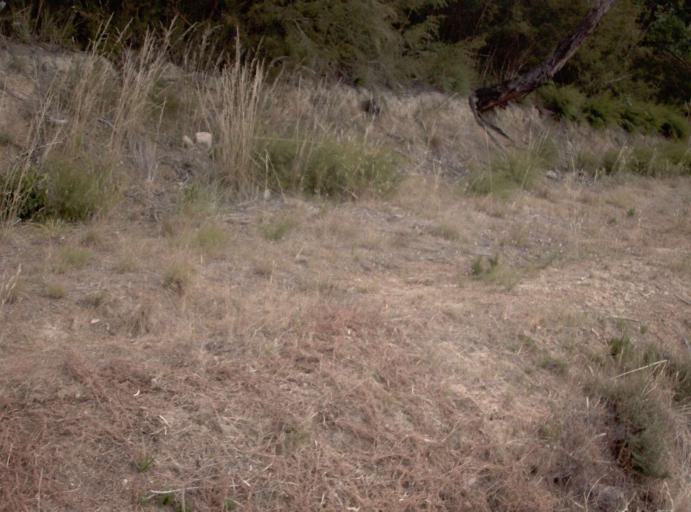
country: AU
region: Victoria
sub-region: Yarra Ranges
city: Lysterfield
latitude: -37.9251
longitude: 145.2853
